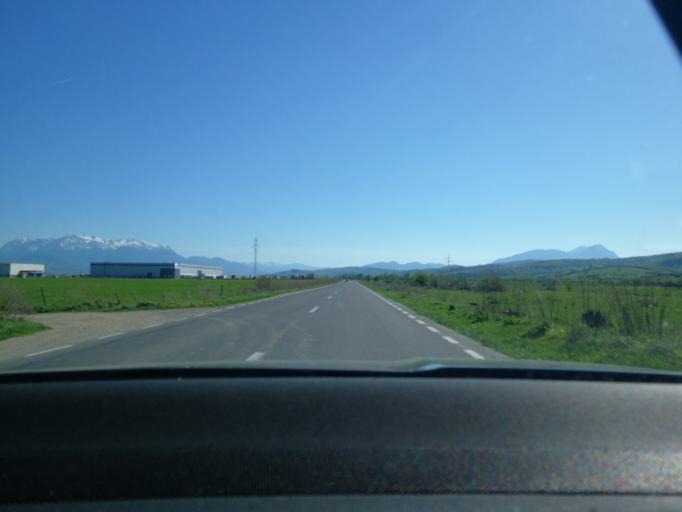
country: RO
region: Brasov
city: Codlea
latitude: 45.6813
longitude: 25.4465
